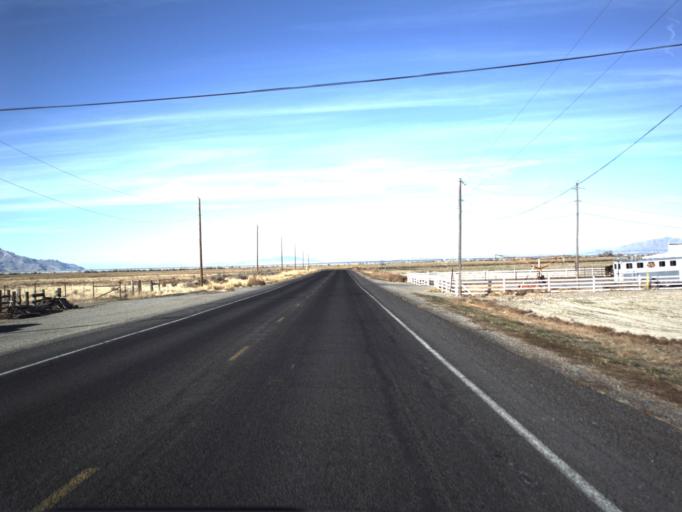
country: US
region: Utah
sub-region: Tooele County
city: Erda
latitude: 40.6090
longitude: -112.3709
